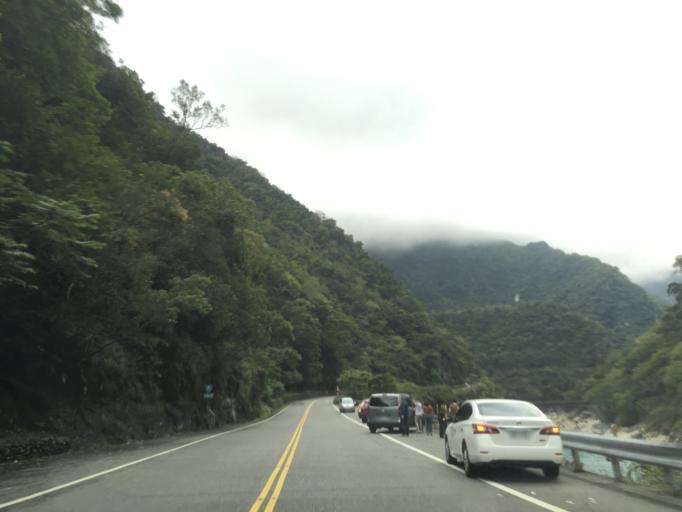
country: TW
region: Taiwan
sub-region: Hualien
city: Hualian
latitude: 24.1762
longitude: 121.5836
